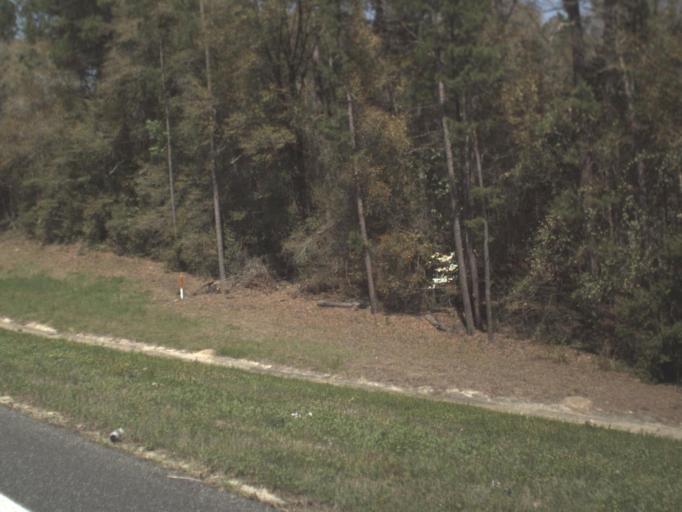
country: US
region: Florida
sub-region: Gadsden County
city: Midway
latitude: 30.5209
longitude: -84.4678
